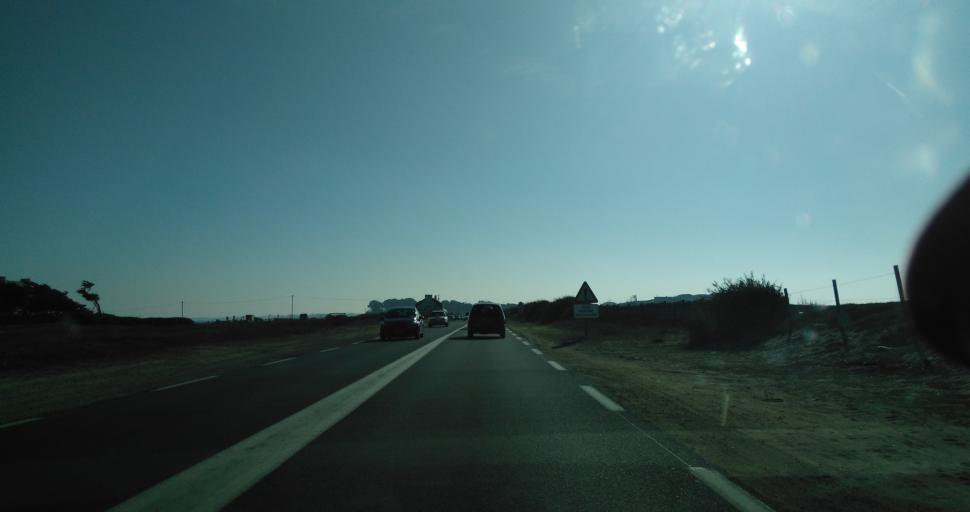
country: FR
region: Brittany
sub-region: Departement du Morbihan
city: Saint-Pierre-Quiberon
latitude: 47.5507
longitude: -3.1342
